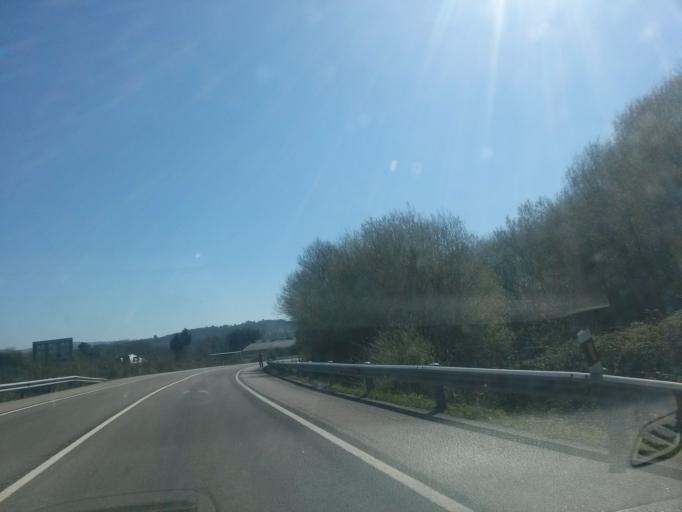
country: ES
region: Galicia
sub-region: Provincia de Lugo
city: Lugo
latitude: 43.0332
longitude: -7.5402
